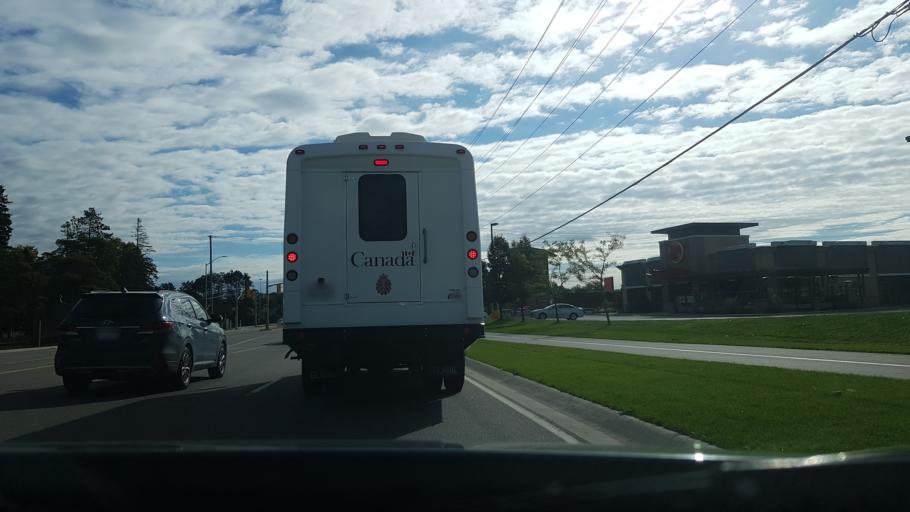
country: CA
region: Ontario
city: Orillia
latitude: 44.6116
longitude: -79.4527
